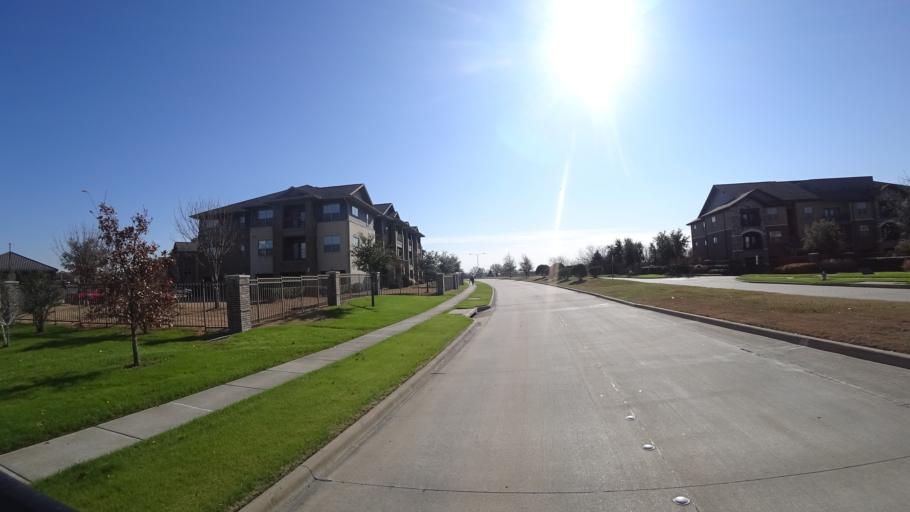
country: US
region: Texas
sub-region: Denton County
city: Lewisville
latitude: 33.0039
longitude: -97.0188
